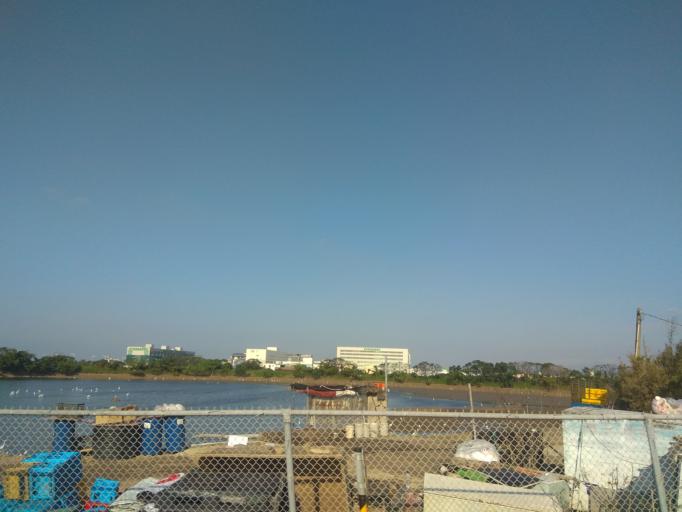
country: TW
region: Taiwan
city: Taoyuan City
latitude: 25.0597
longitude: 121.2145
